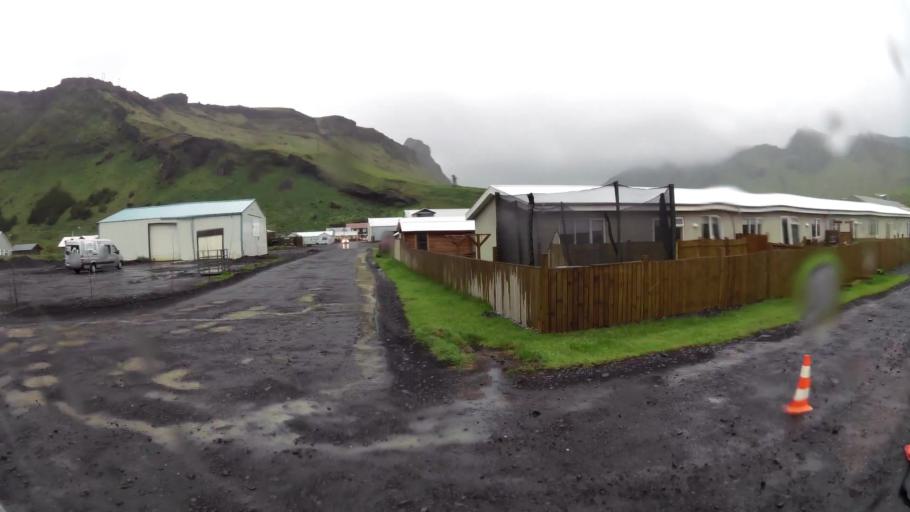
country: IS
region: South
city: Vestmannaeyjar
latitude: 63.4162
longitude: -19.0123
